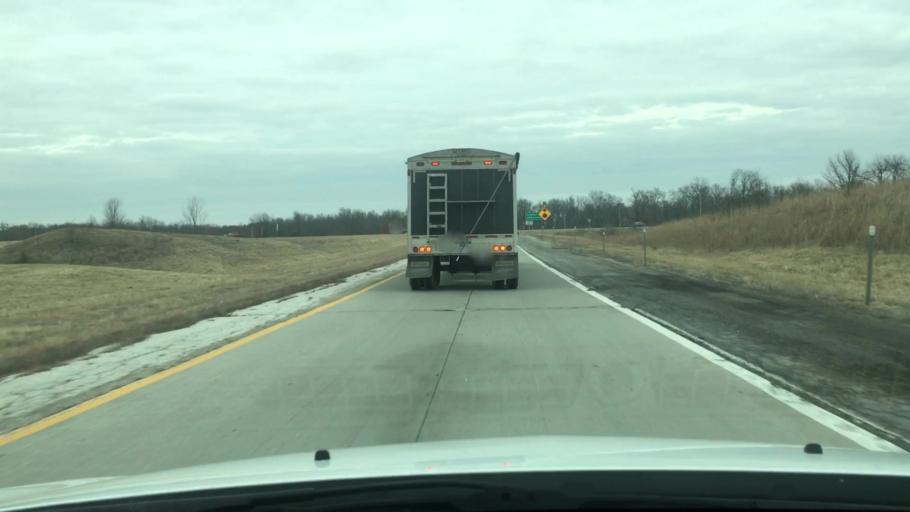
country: US
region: Missouri
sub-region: Audrain County
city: Mexico
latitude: 39.1611
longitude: -91.8420
